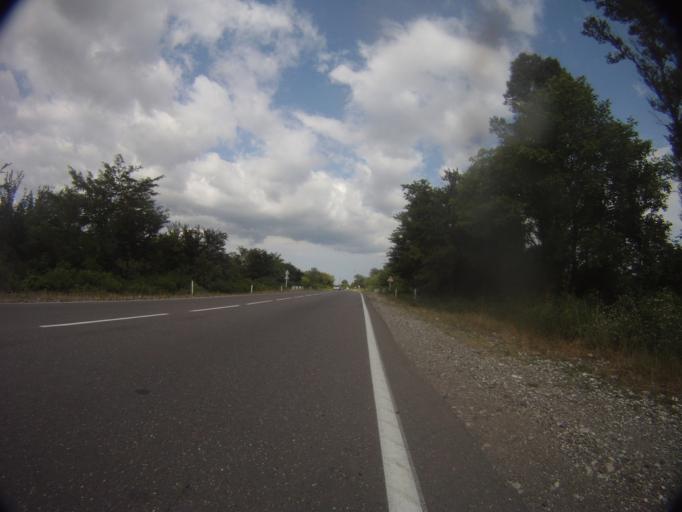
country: GE
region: Imereti
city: Samtredia
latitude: 42.1653
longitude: 42.3637
